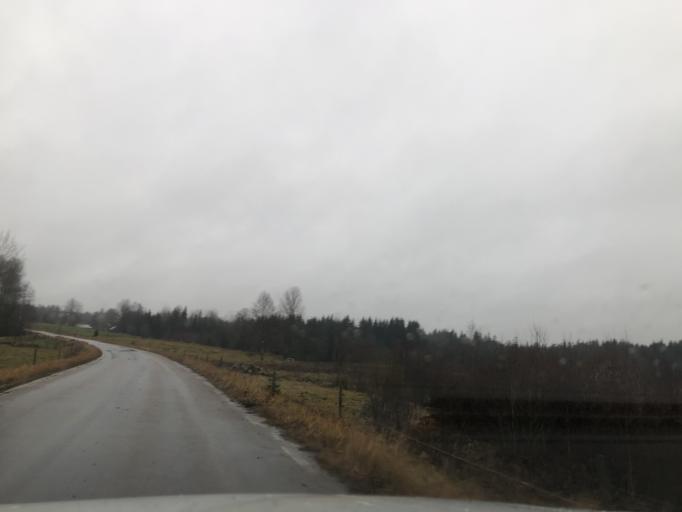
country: SE
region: Vaestra Goetaland
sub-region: Ulricehamns Kommun
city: Ulricehamn
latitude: 57.8574
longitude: 13.5499
